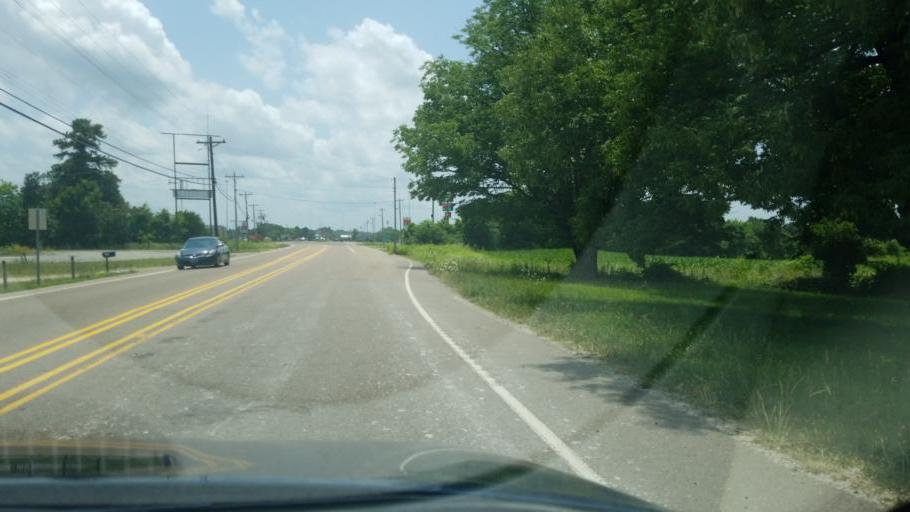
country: US
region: Tennessee
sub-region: Madison County
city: Jackson
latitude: 35.6848
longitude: -88.7394
